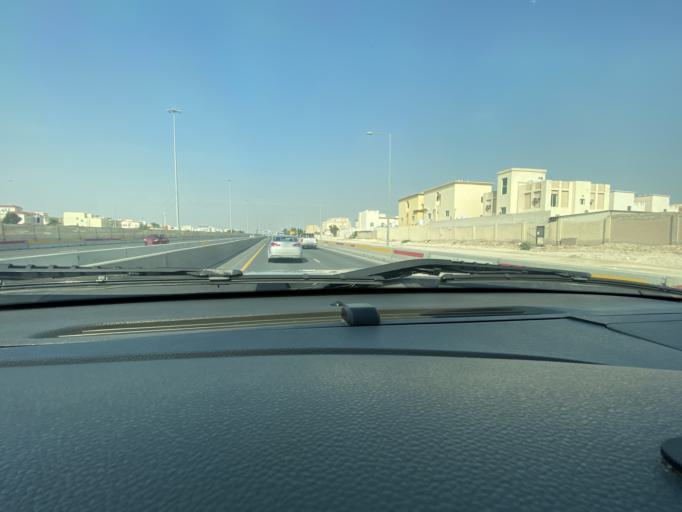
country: QA
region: Baladiyat ad Dawhah
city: Doha
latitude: 25.2441
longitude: 51.5156
